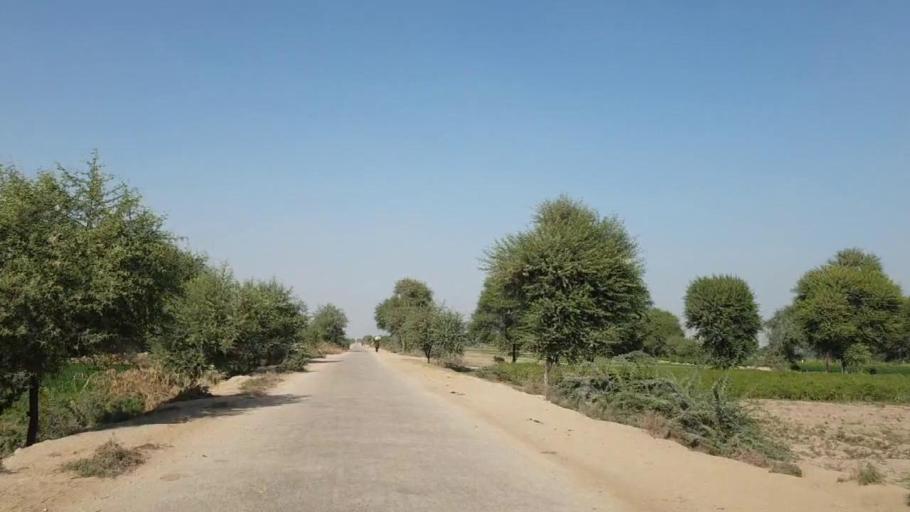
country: PK
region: Sindh
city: Digri
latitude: 25.0078
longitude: 69.1063
